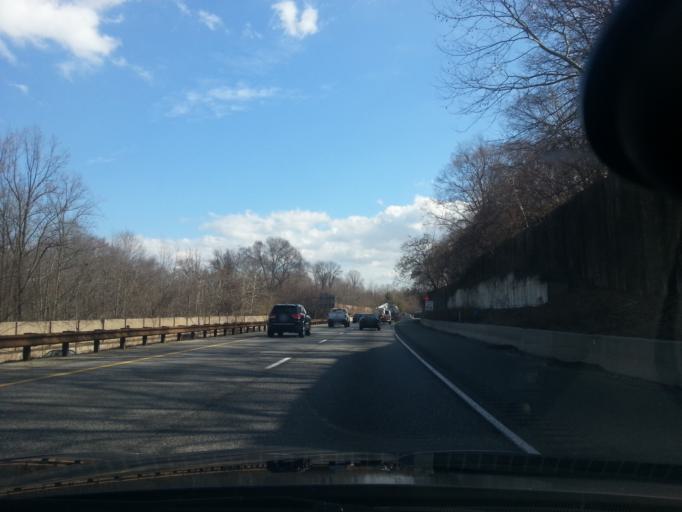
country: US
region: Pennsylvania
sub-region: Delaware County
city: Broomall
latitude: 39.9700
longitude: -75.3371
